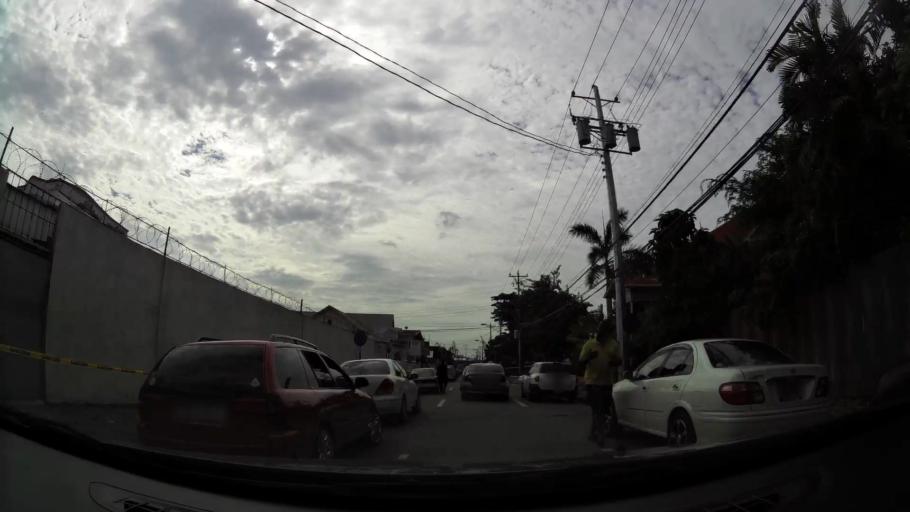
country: TT
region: City of Port of Spain
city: Port-of-Spain
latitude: 10.6549
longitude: -61.5142
